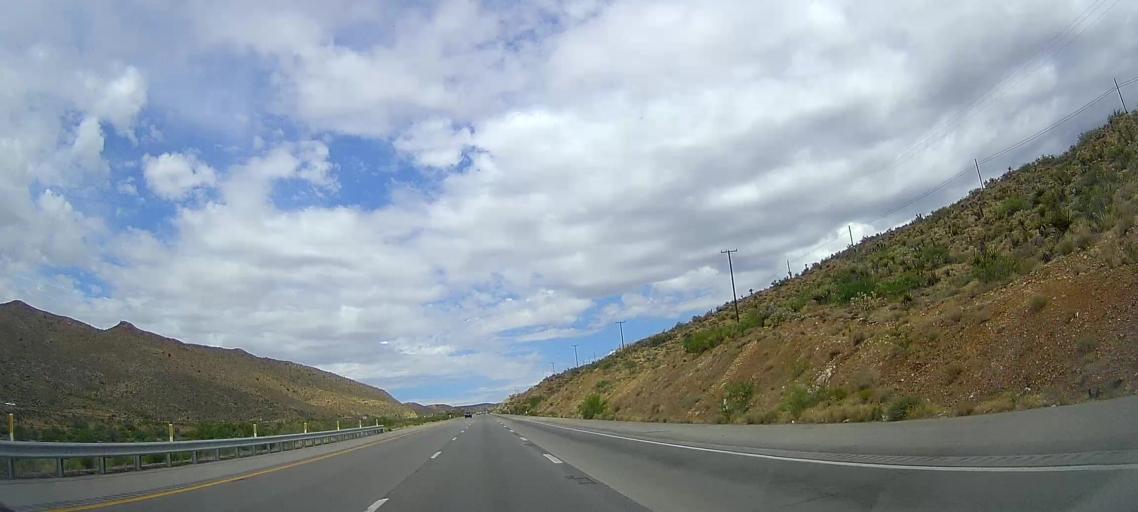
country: US
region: Nevada
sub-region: Clark County
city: Sandy Valley
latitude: 35.4680
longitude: -115.4897
